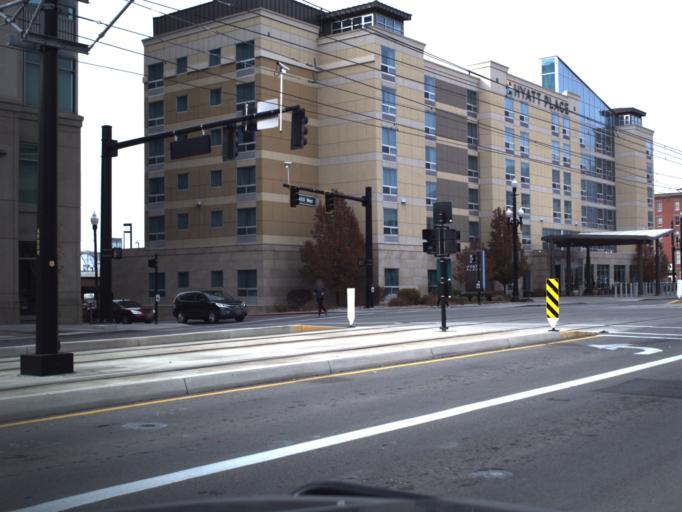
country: US
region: Utah
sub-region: Salt Lake County
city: Salt Lake City
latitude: 40.7701
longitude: -111.9024
